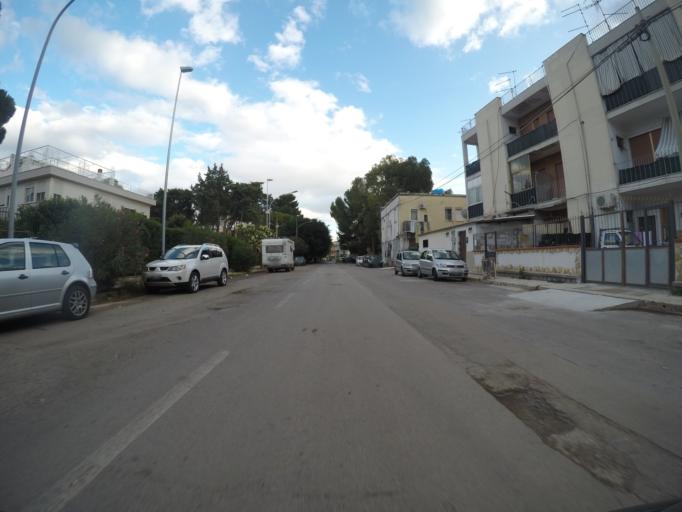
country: IT
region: Sicily
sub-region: Palermo
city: Isola delle Femmine
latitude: 38.1995
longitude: 13.3094
